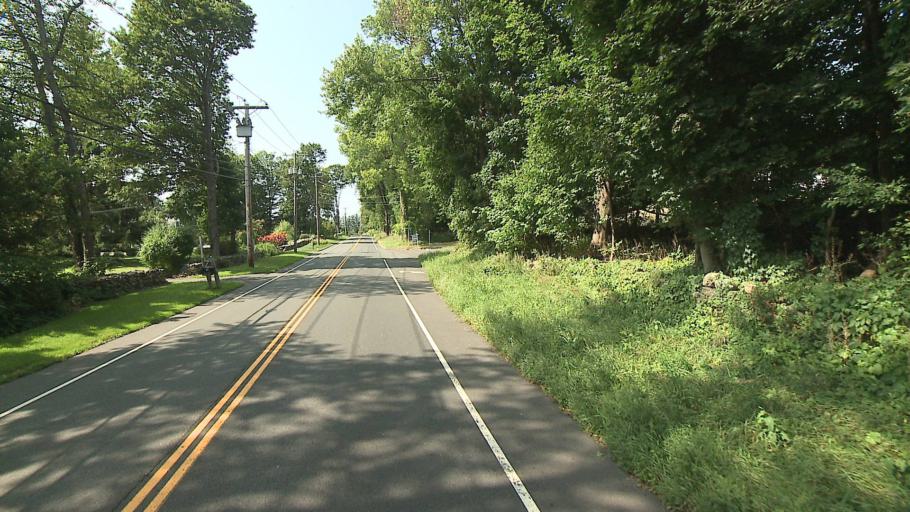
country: US
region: Connecticut
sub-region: Fairfield County
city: Newtown
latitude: 41.4416
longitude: -73.3714
